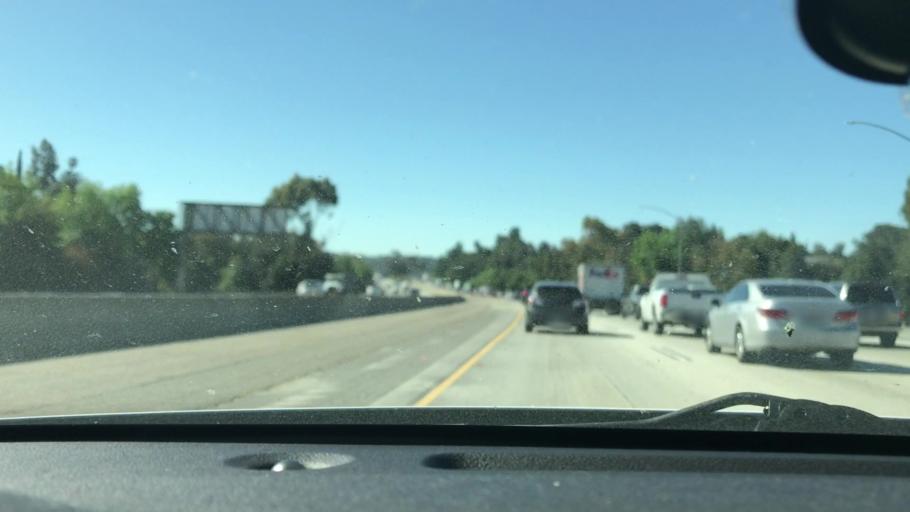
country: US
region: California
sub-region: Los Angeles County
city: Diamond Bar
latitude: 34.0298
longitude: -117.8110
